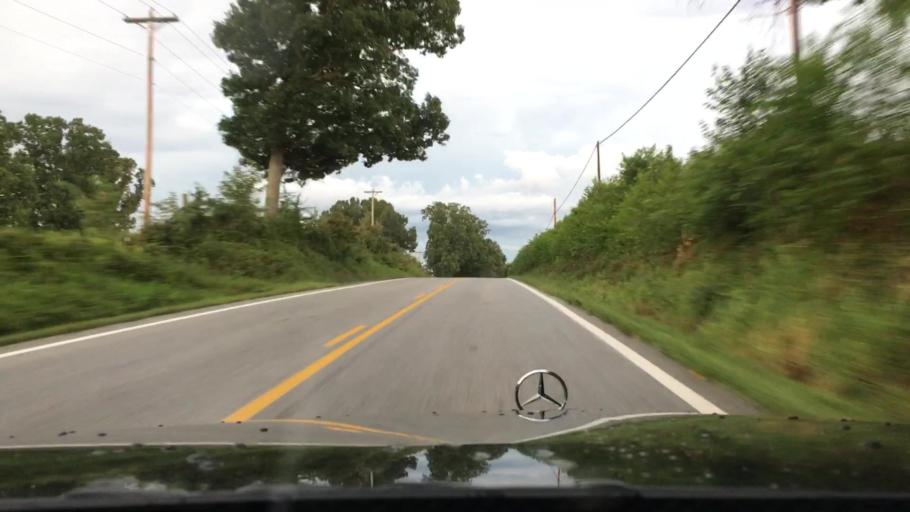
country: US
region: Virginia
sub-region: Amherst County
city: Amherst
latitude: 37.6296
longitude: -79.0186
